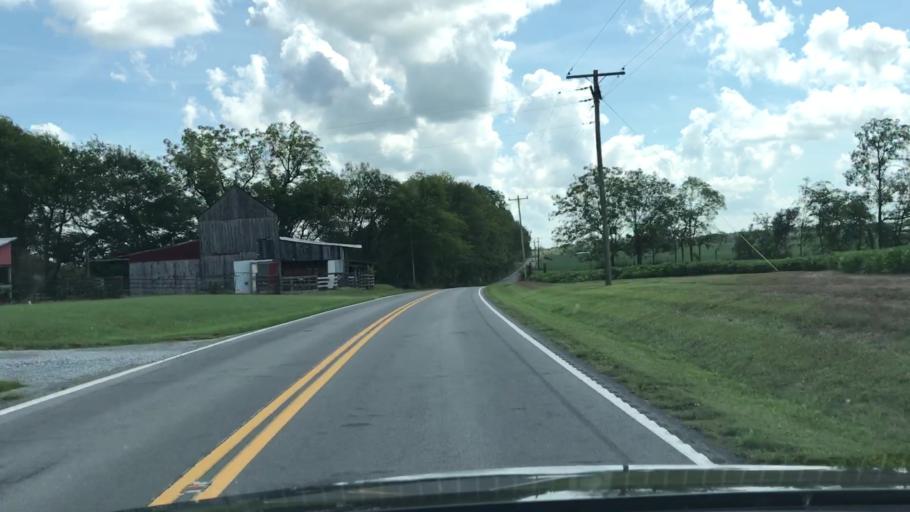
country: US
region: Tennessee
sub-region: Robertson County
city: Springfield
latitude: 36.5750
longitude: -86.8682
